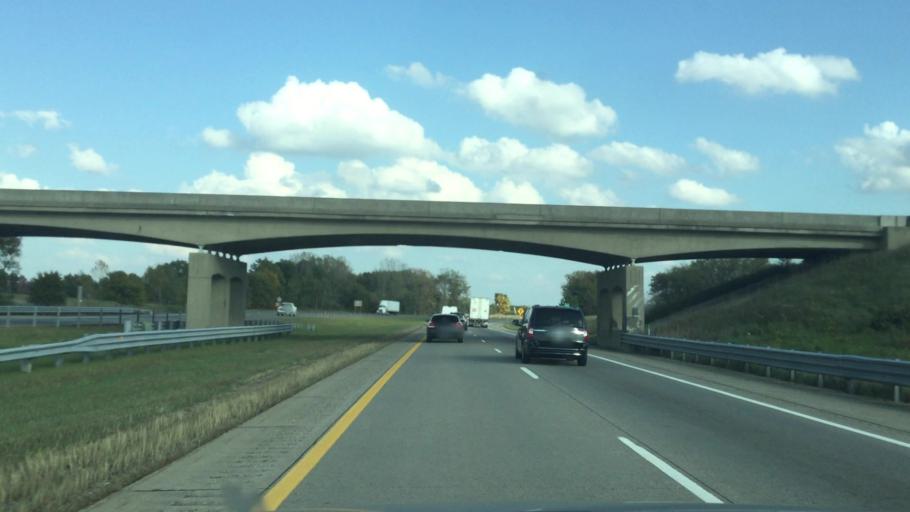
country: US
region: Michigan
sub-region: Calhoun County
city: Albion
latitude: 42.2836
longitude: -84.8014
